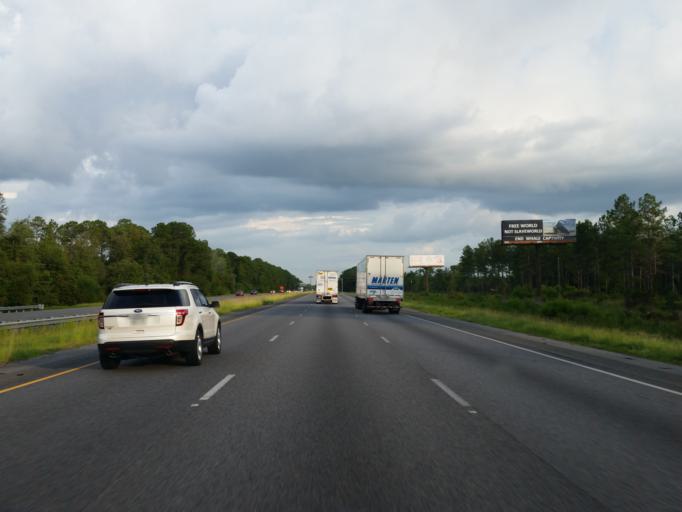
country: US
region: Georgia
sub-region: Lowndes County
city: Valdosta
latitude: 30.7683
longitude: -83.2888
